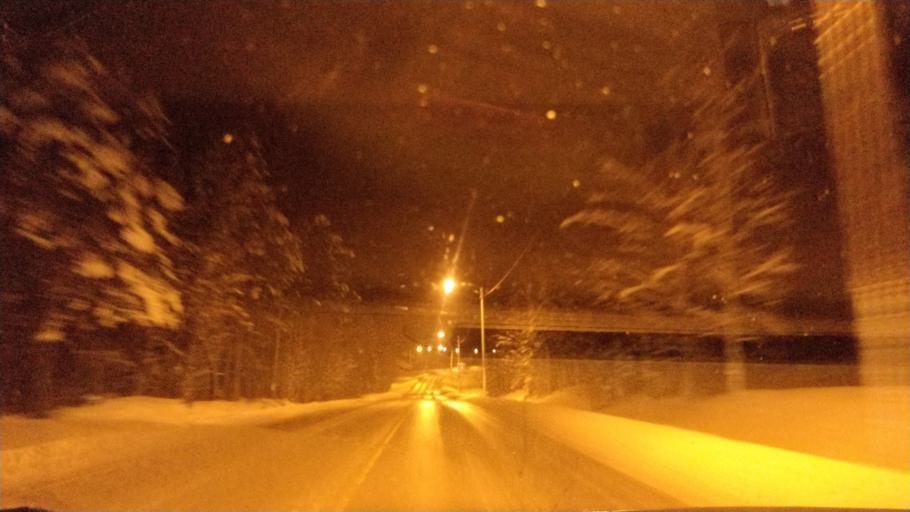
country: FI
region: Lapland
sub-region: Rovaniemi
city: Rovaniemi
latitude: 66.3197
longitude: 25.3593
